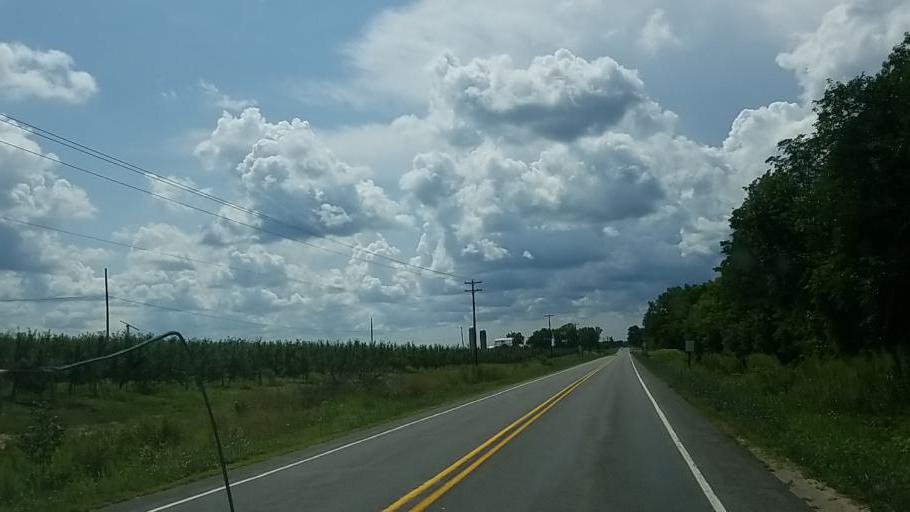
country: US
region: Michigan
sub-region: Kent County
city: Sparta
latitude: 43.1166
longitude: -85.7687
